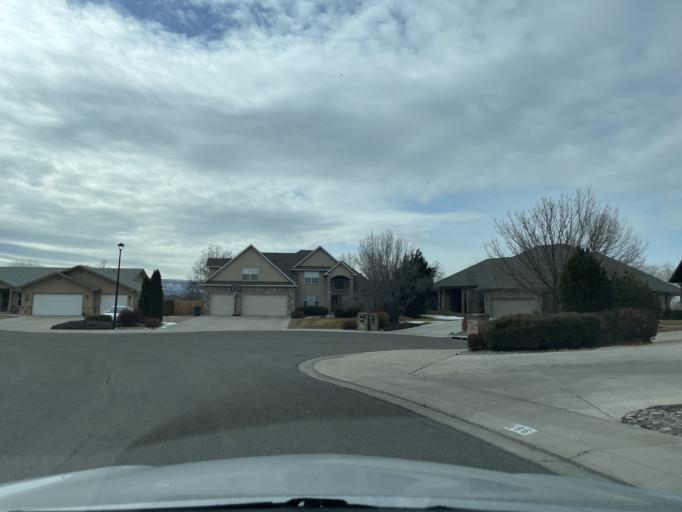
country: US
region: Colorado
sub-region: Mesa County
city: Grand Junction
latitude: 39.1051
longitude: -108.5842
